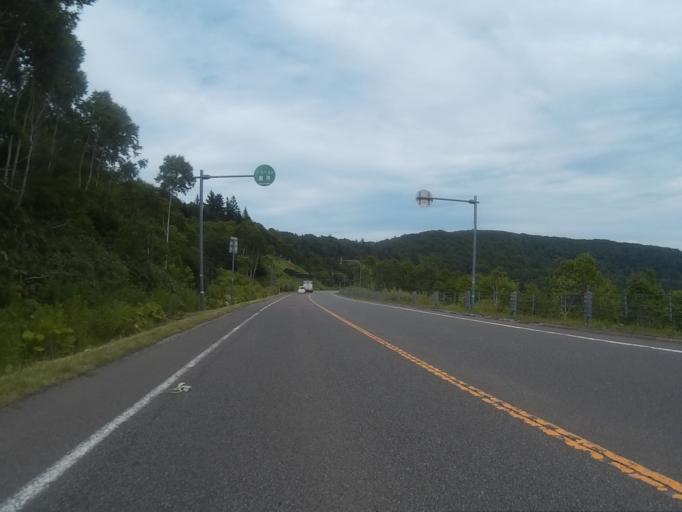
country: JP
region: Hokkaido
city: Sapporo
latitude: 42.8668
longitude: 141.1104
